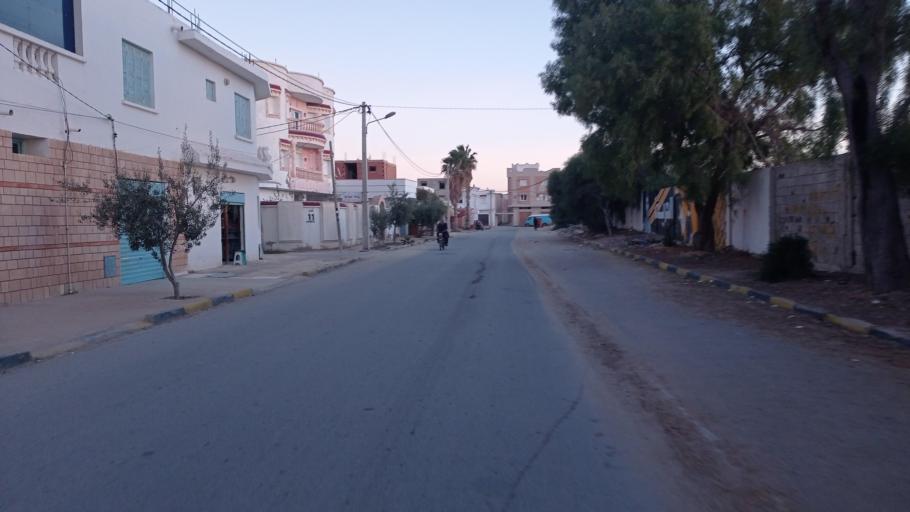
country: TN
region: Qabis
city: Gabes
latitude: 33.8449
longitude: 10.1163
